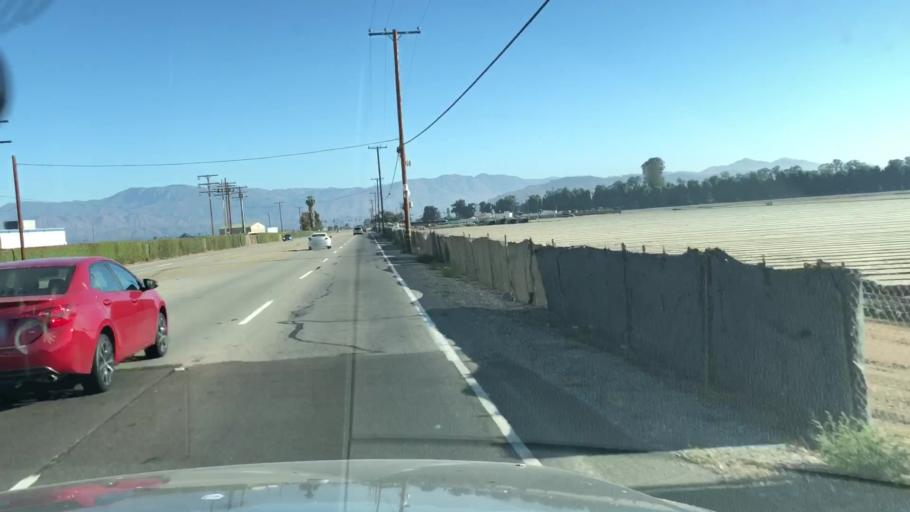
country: US
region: California
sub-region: Ventura County
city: El Rio
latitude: 34.2391
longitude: -119.1520
